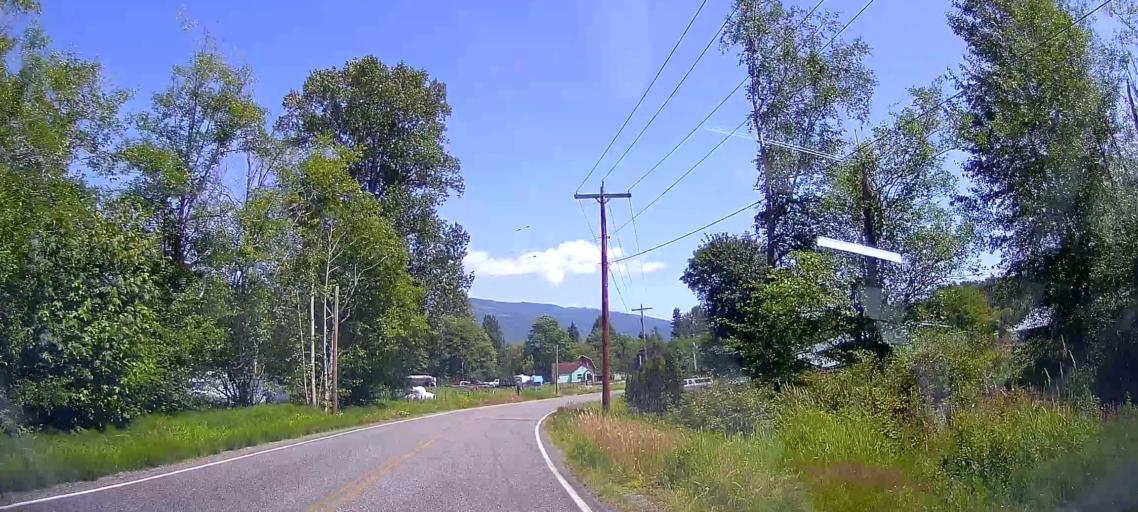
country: US
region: Washington
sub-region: Skagit County
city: Sedro-Woolley
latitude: 48.5842
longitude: -122.2897
